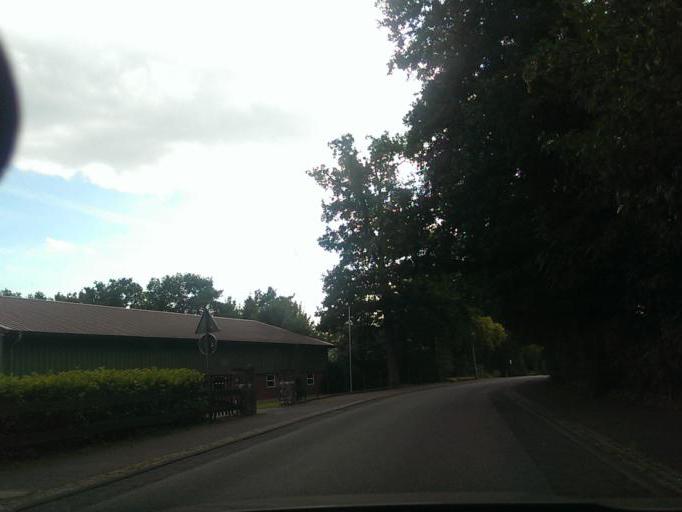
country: DE
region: North Rhine-Westphalia
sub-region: Regierungsbezirk Detmold
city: Delbruck
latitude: 51.7298
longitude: 8.5661
